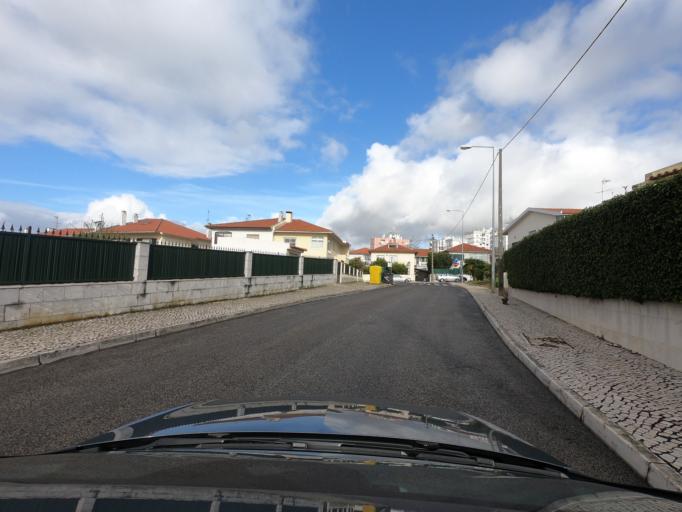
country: PT
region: Lisbon
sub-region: Cascais
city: Sao Domingos de Rana
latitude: 38.6989
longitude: -9.3250
